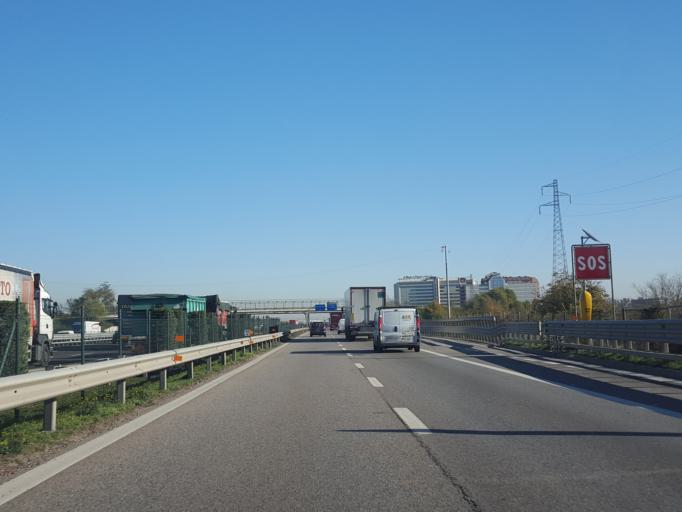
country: IT
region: Veneto
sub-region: Provincia di Verona
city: San Giovanni Lupatoto
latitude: 45.3992
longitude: 11.0054
